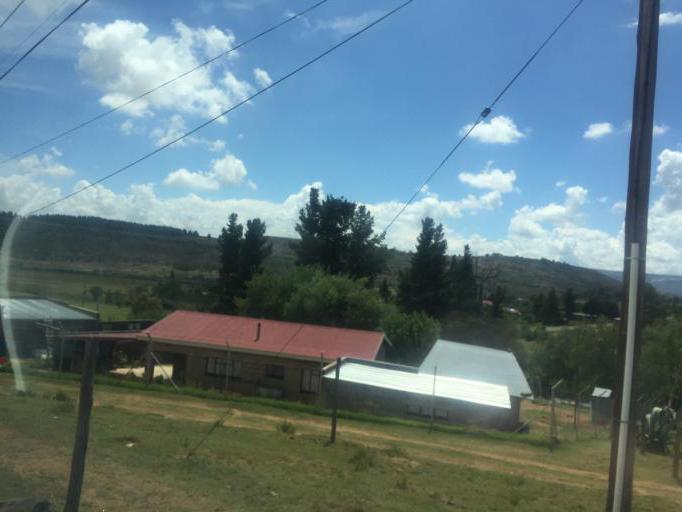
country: LS
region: Maseru
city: Nako
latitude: -29.6232
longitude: 27.5153
